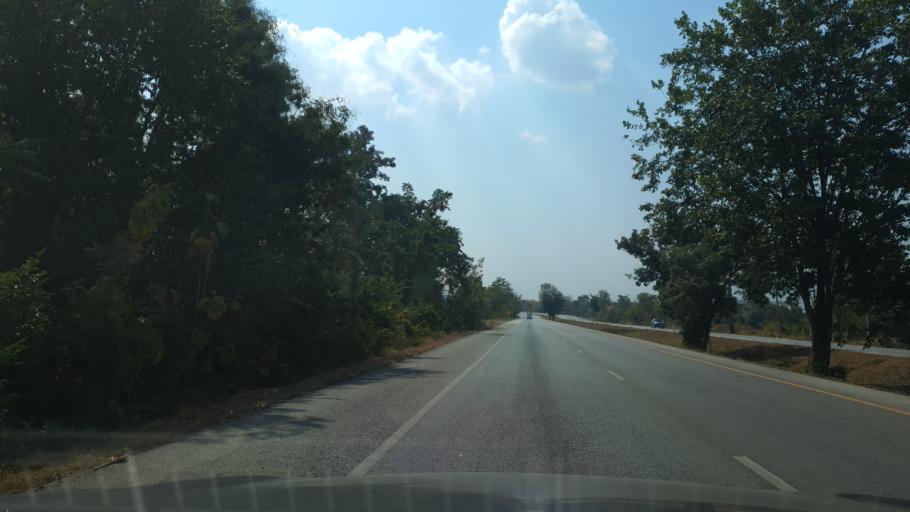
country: TH
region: Lampang
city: Mae Phrik
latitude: 17.4138
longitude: 99.1537
